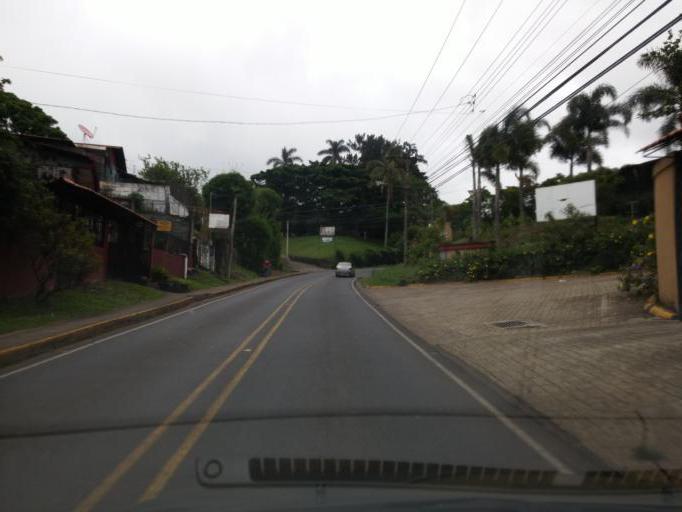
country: CR
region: Heredia
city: Mercedes
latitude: 10.0293
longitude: -84.1226
